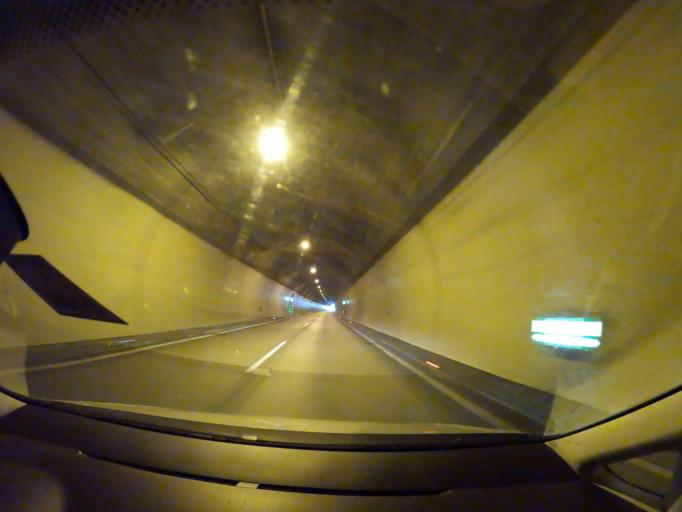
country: AT
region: Styria
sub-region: Politischer Bezirk Voitsberg
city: Pack
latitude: 46.9524
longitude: 15.0081
